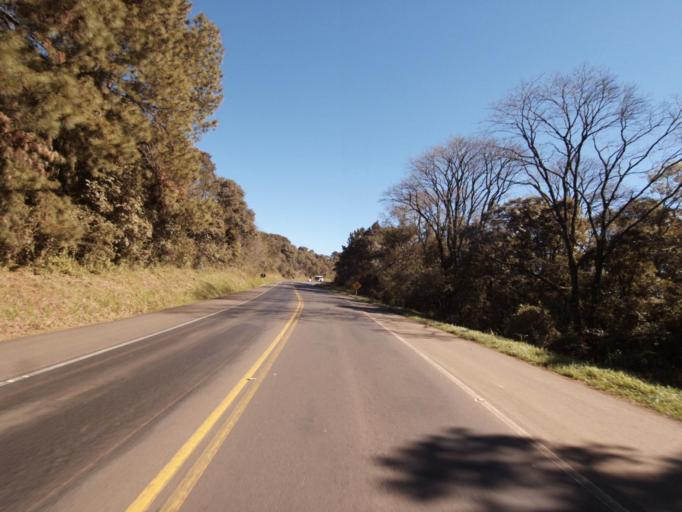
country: BR
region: Santa Catarina
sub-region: Joacaba
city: Joacaba
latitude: -27.1585
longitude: -51.5872
